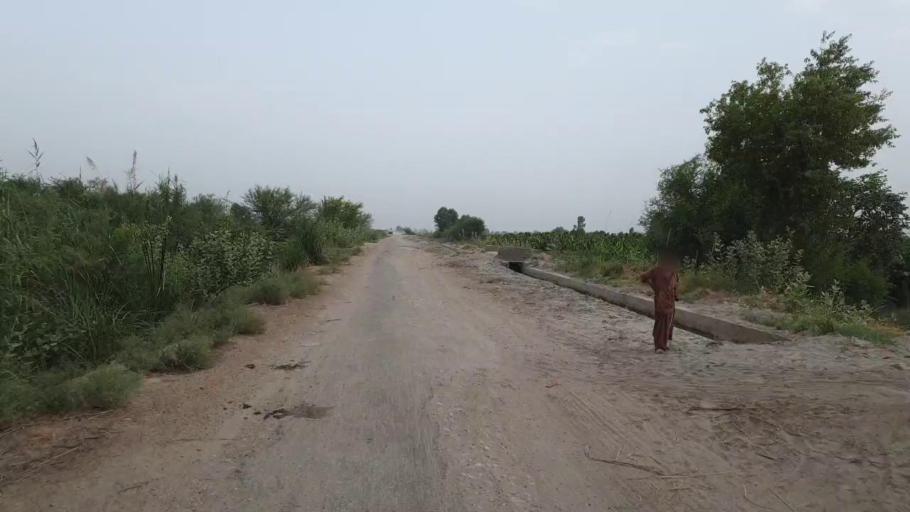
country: PK
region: Sindh
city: Daur
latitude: 26.4167
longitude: 68.2251
